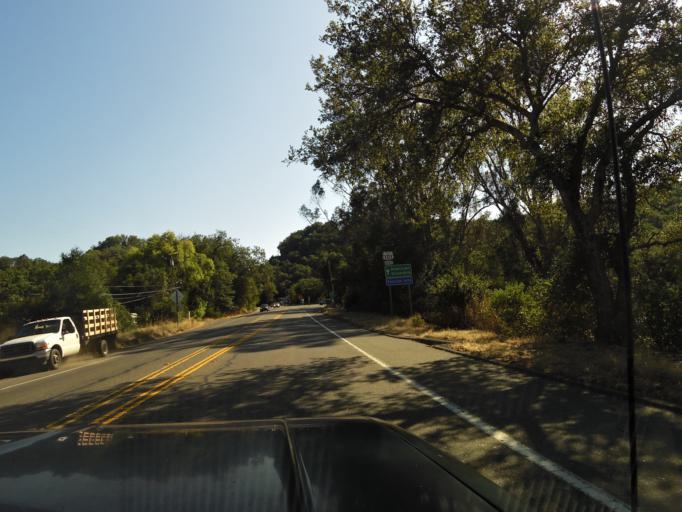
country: US
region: California
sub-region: Sonoma County
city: Cloverdale
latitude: 38.8202
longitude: -123.0213
